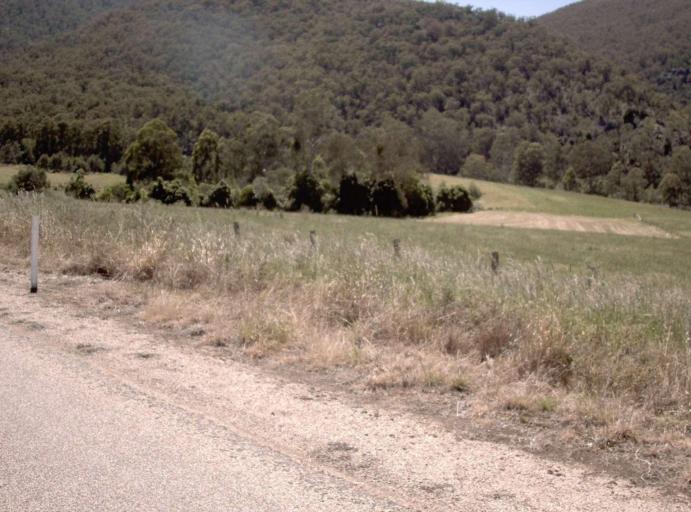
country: AU
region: Victoria
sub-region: East Gippsland
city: Lakes Entrance
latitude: -37.3961
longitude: 148.2161
